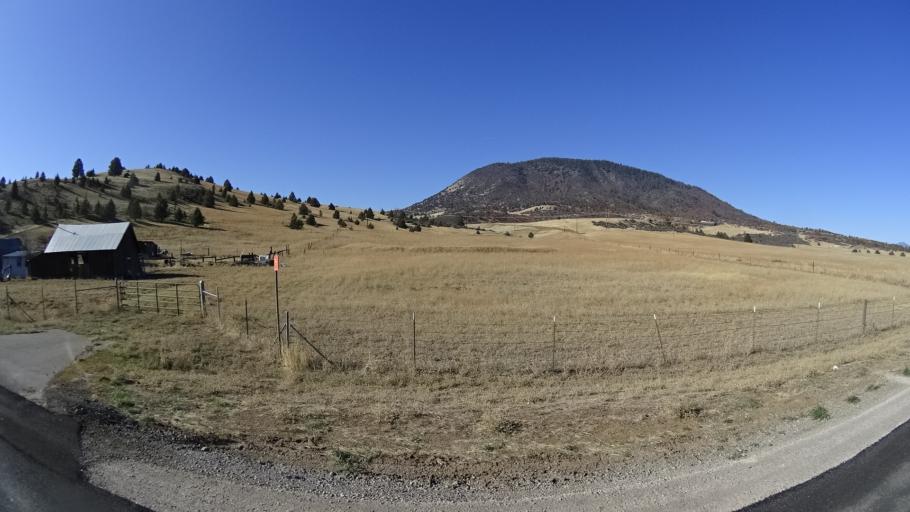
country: US
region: California
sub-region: Siskiyou County
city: Montague
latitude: 41.8551
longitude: -122.4654
